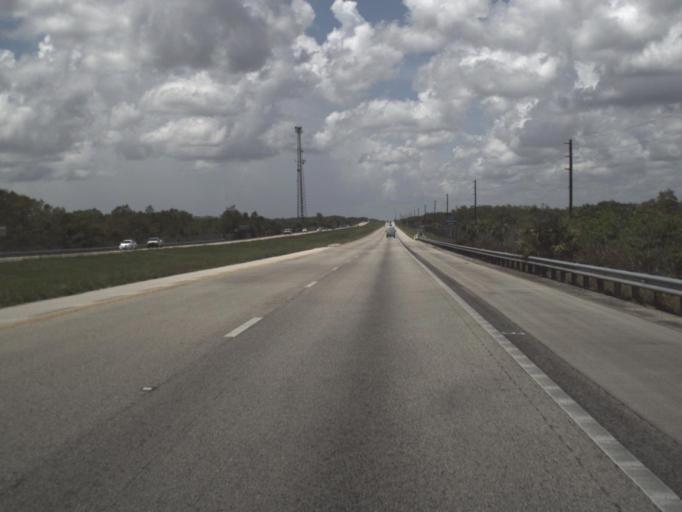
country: US
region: Florida
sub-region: Broward County
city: Weston
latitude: 26.1729
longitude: -80.8782
